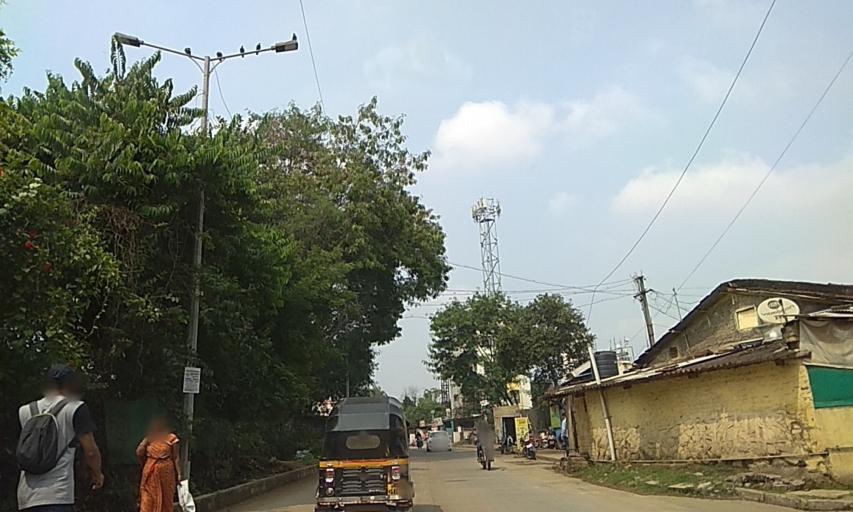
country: IN
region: Maharashtra
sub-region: Pune Division
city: Pimpri
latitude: 18.5597
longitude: 73.7848
